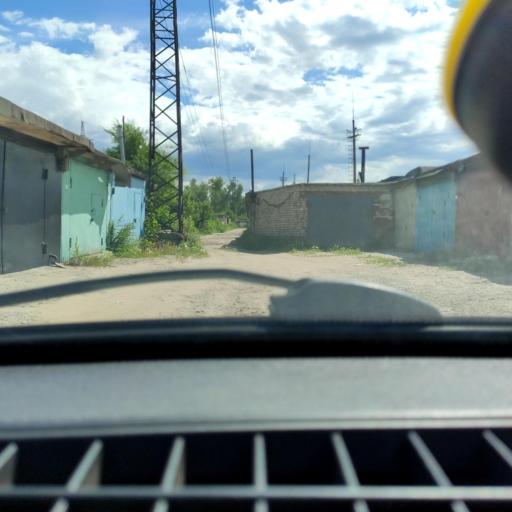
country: RU
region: Samara
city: Zhigulevsk
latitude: 53.4703
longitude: 49.5181
